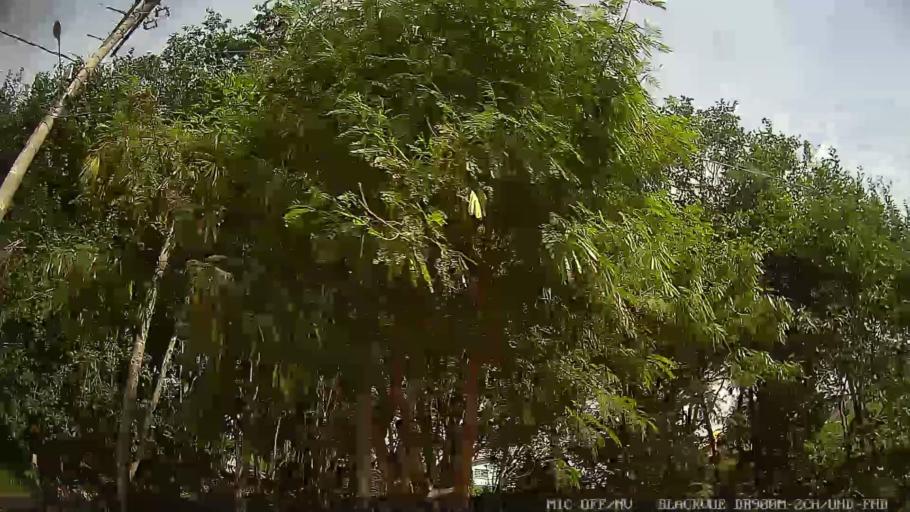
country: BR
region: Sao Paulo
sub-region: Braganca Paulista
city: Braganca Paulista
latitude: -22.9141
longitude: -46.5454
